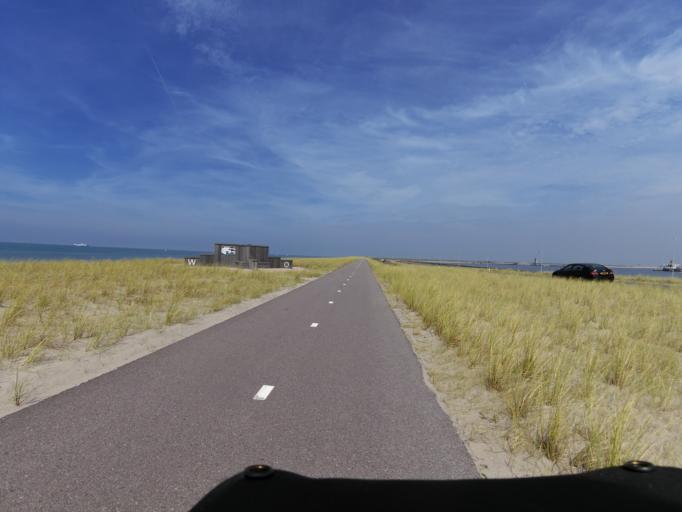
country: NL
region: South Holland
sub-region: Gemeente Goeree-Overflakkee
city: Goedereede
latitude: 51.9723
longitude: 3.9709
